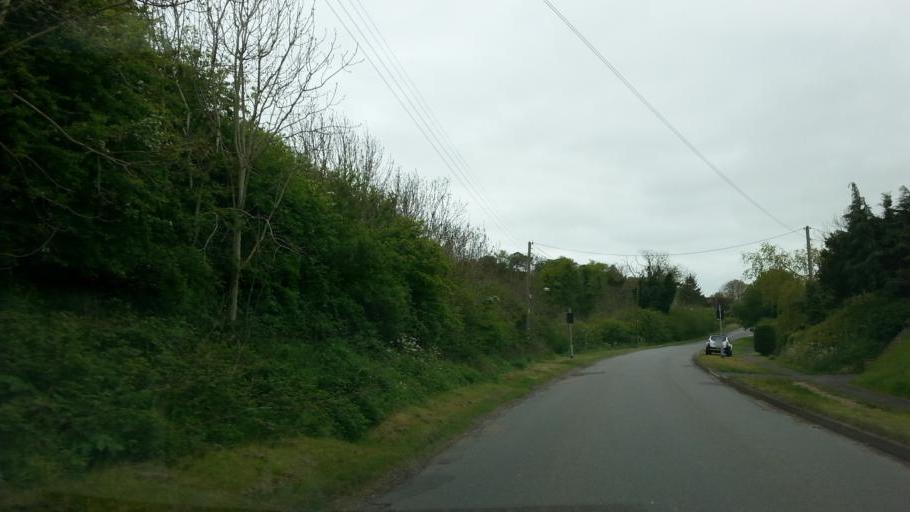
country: GB
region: England
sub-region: District of Rutland
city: Greetham
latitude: 52.8104
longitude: -0.6213
